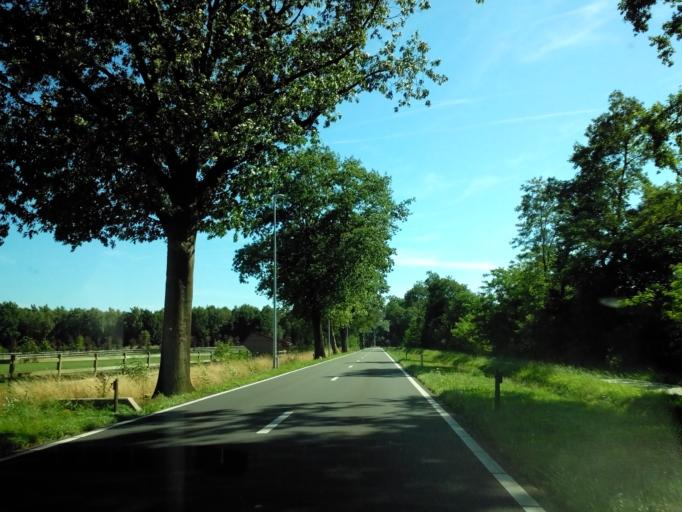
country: BE
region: Flanders
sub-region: Provincie Limburg
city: Opglabbeek
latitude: 51.0686
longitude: 5.5849
